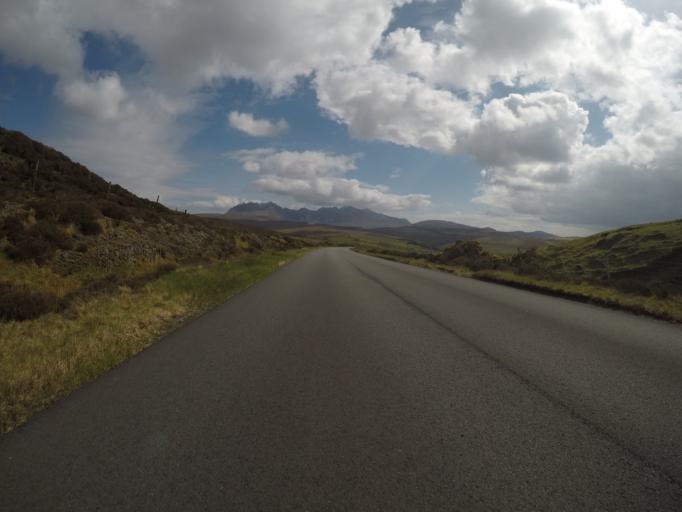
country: GB
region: Scotland
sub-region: Highland
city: Isle of Skye
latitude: 57.3080
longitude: -6.3165
